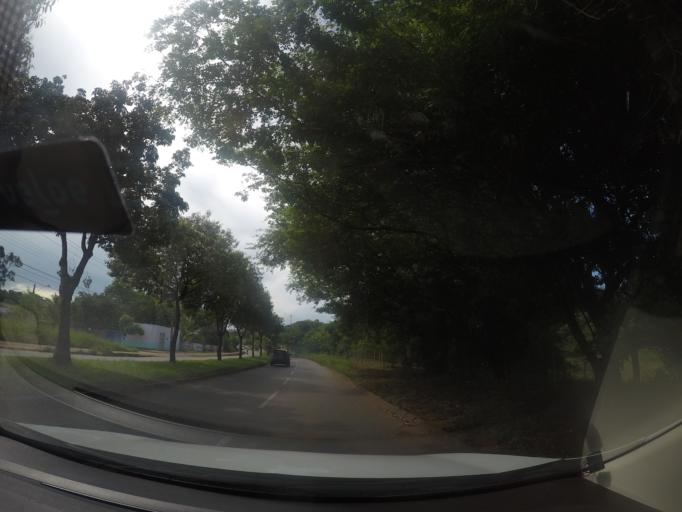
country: BR
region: Goias
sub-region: Trindade
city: Trindade
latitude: -16.6710
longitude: -49.3858
